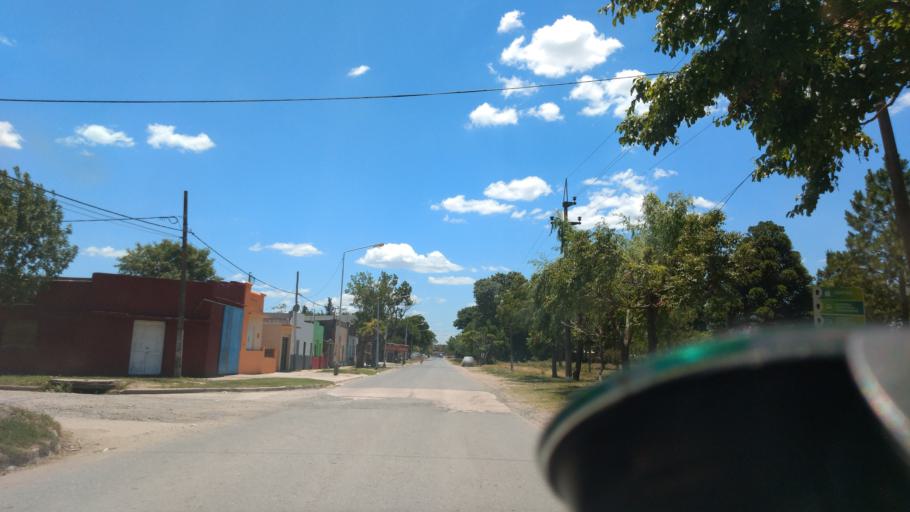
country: AR
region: Santa Fe
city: Laguna Paiva
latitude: -31.3120
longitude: -60.6584
